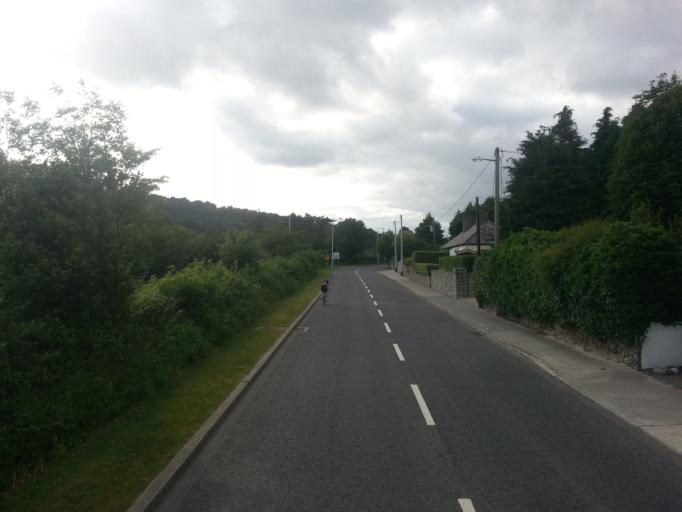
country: IE
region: Leinster
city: Sandyford
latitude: 53.2502
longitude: -6.2090
